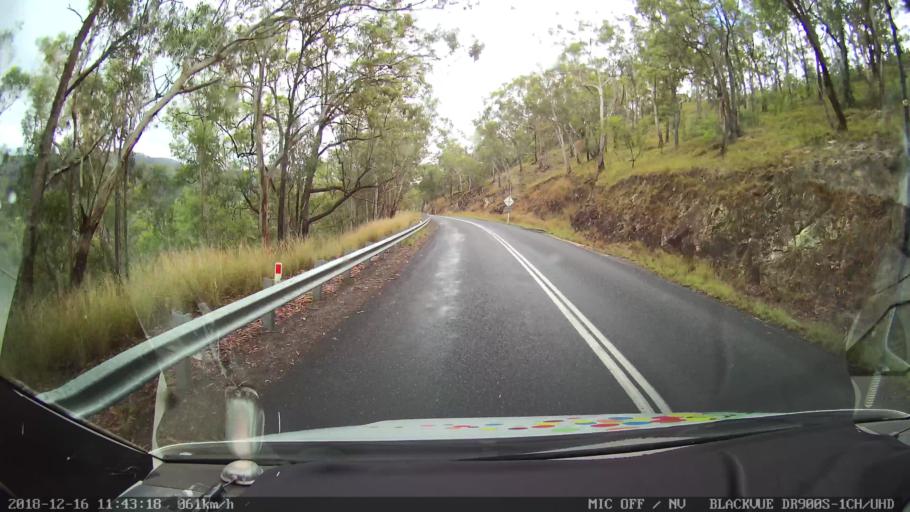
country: AU
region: New South Wales
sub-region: Tenterfield Municipality
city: Carrolls Creek
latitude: -28.9464
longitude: 152.2161
